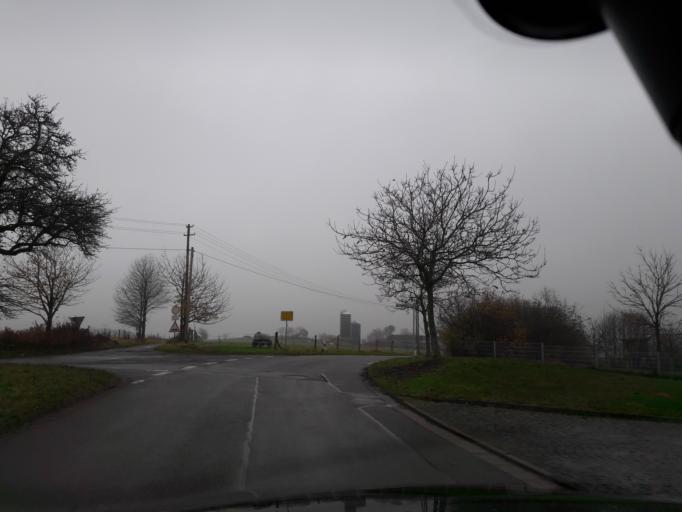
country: DE
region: Rheinland-Pfalz
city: Wahnwegen
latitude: 49.4733
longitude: 7.3886
